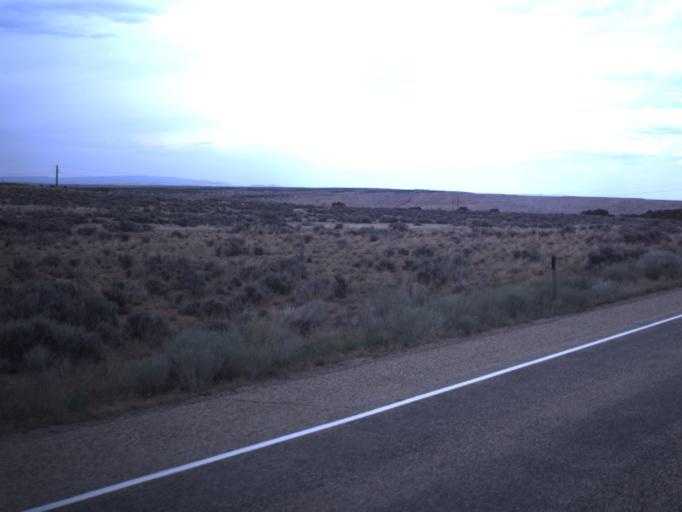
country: US
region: Utah
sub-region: Uintah County
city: Naples
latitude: 40.1428
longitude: -109.2834
